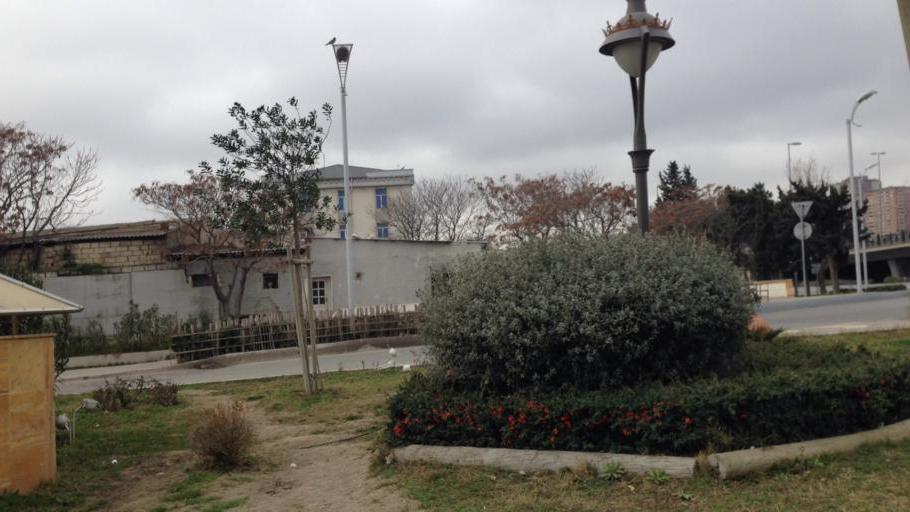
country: AZ
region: Baki
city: Bilajari
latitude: 40.4099
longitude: 49.8348
